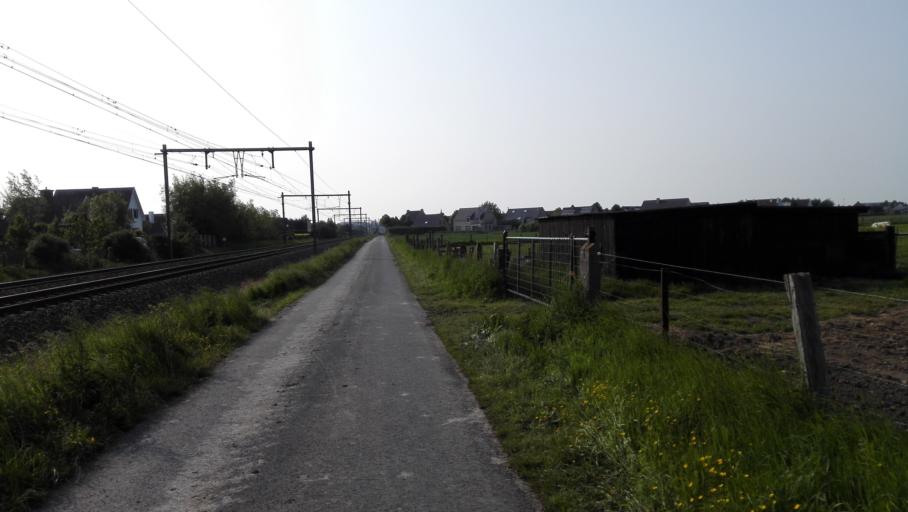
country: BE
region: Flanders
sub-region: Provincie West-Vlaanderen
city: Blankenberge
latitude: 51.3008
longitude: 3.1521
